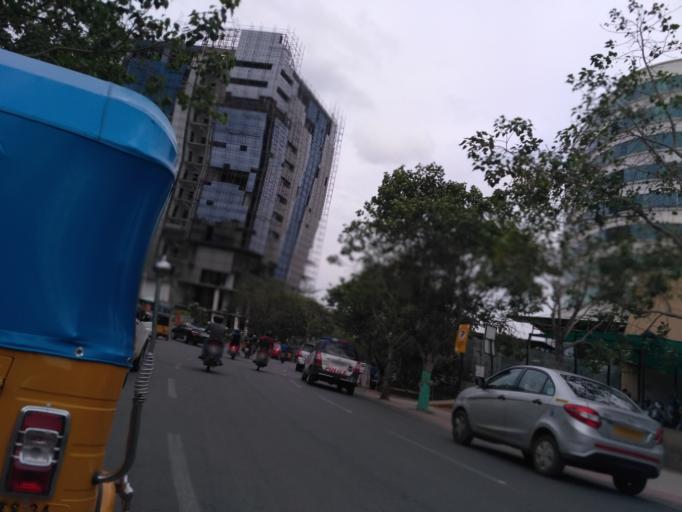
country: IN
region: Telangana
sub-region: Rangareddi
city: Kukatpalli
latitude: 17.4333
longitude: 78.3860
